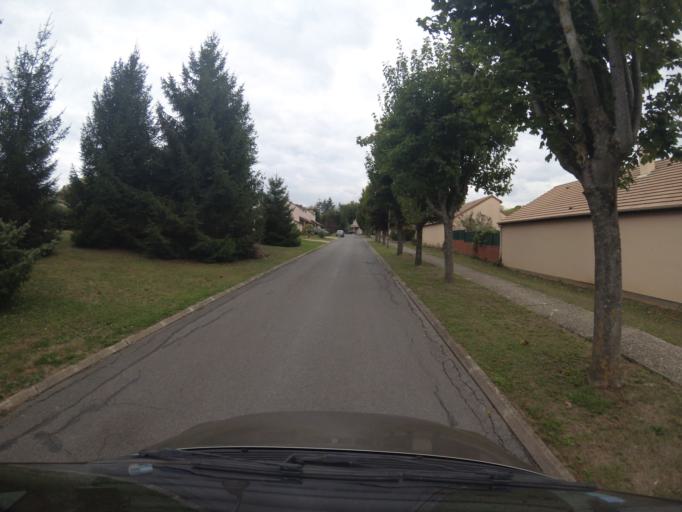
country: FR
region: Ile-de-France
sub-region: Departement de Seine-et-Marne
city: Collegien
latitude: 48.8514
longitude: 2.6729
